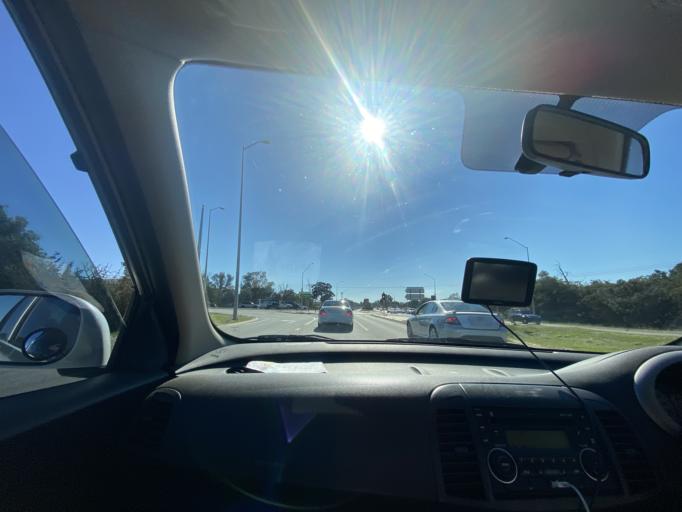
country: AU
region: Western Australia
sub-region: Swan
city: Bellevue
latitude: -31.9167
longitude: 116.0145
